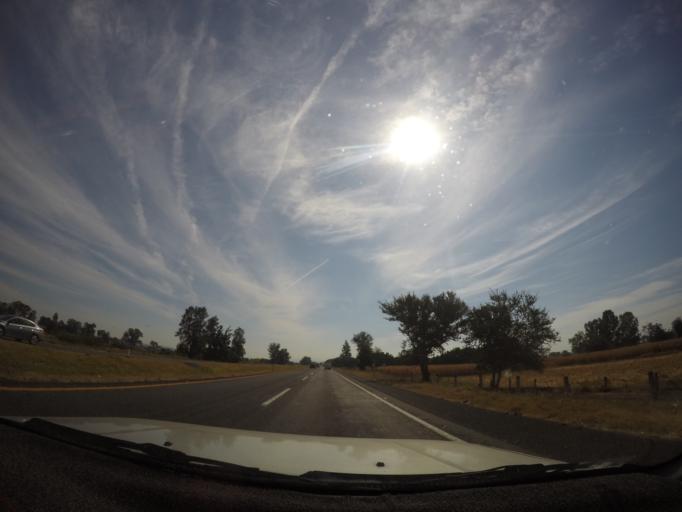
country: MX
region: Michoacan
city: Vistahermosa de Negrete
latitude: 20.2774
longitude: -102.4515
